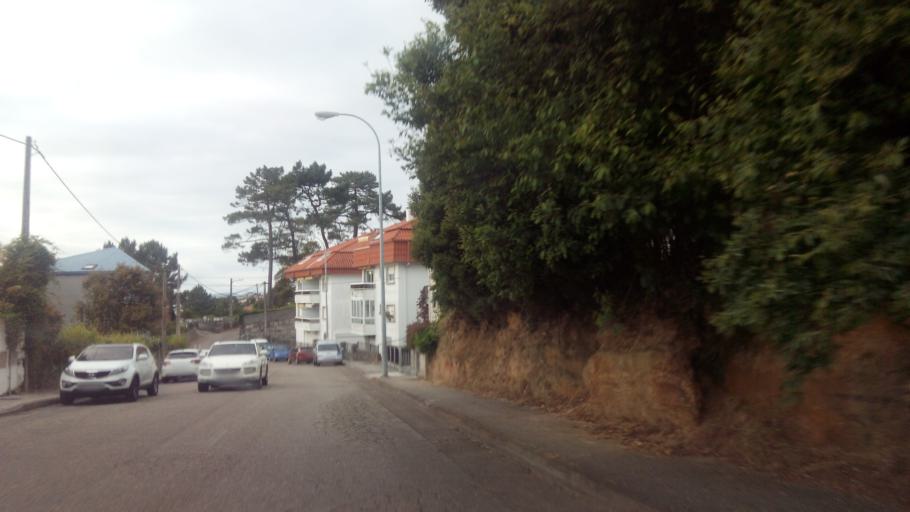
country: ES
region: Galicia
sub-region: Provincia de Pontevedra
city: Nigran
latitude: 42.1237
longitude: -8.8170
